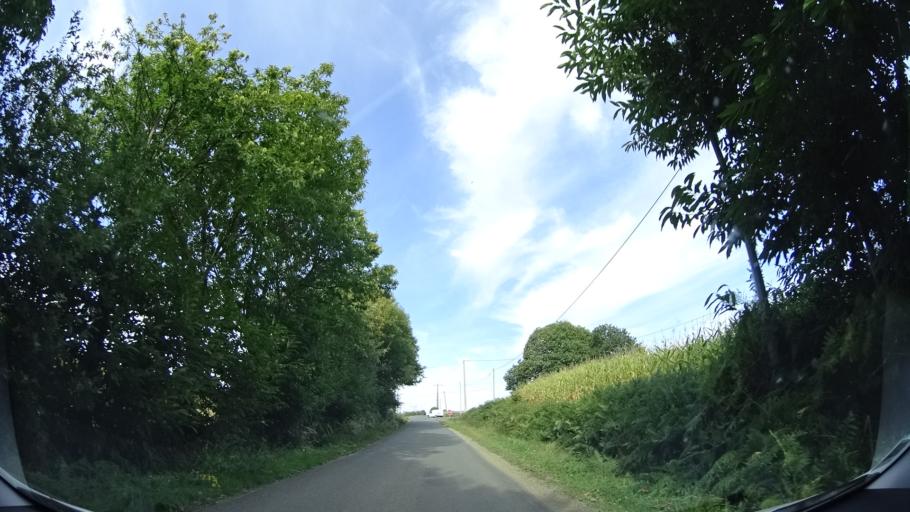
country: FR
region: Brittany
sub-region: Departement d'Ille-et-Vilaine
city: Romagne
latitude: 48.3221
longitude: -1.2716
